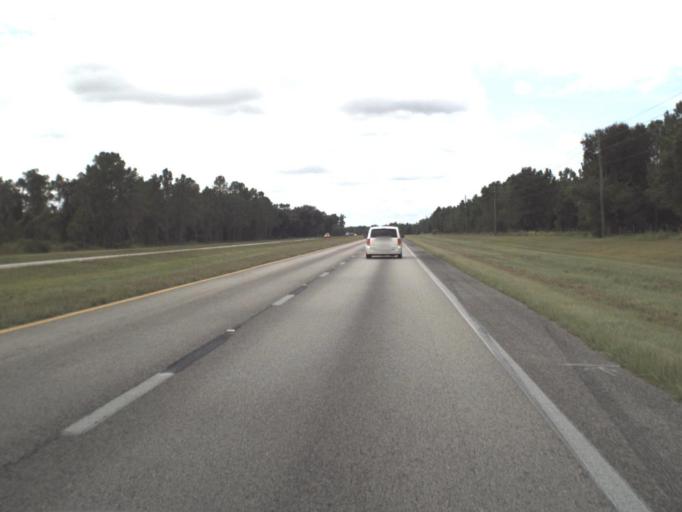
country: US
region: Florida
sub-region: Polk County
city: Fort Meade
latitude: 27.7028
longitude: -81.8091
